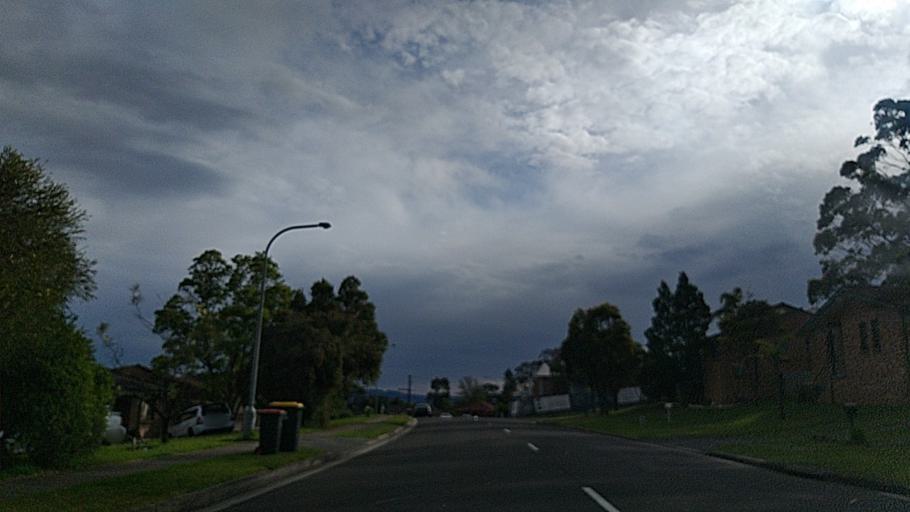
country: AU
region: New South Wales
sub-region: Wollongong
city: Berkeley
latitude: -34.4771
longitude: 150.8480
